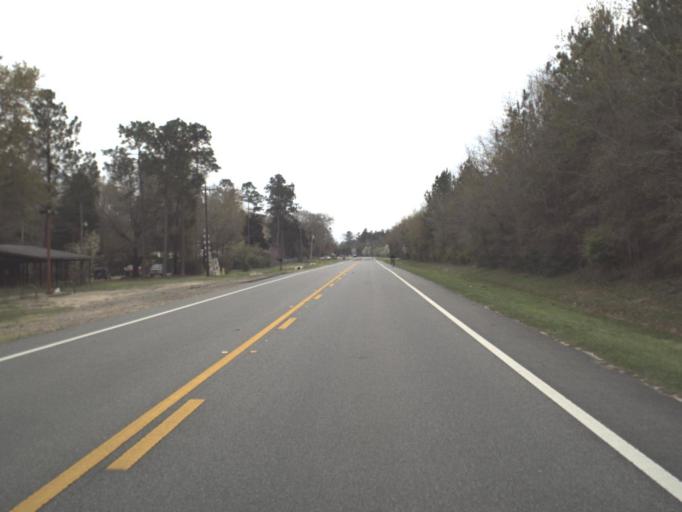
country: US
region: Florida
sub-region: Gulf County
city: Wewahitchka
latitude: 30.2714
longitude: -85.2421
